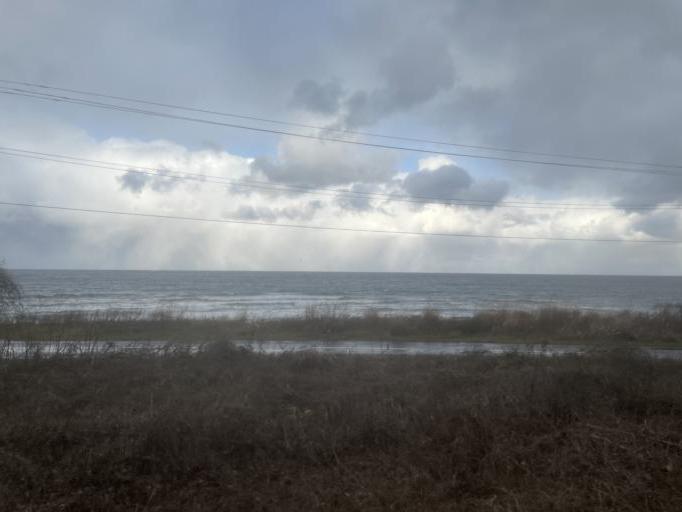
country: JP
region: Aomori
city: Shimokizukuri
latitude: 41.1882
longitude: 140.4546
